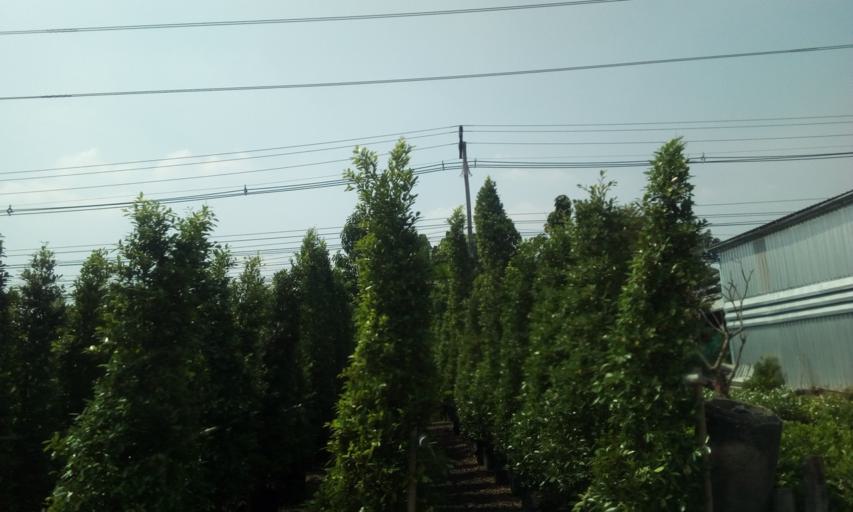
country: TH
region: Nakhon Nayok
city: Ongkharak
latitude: 14.0975
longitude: 100.9439
